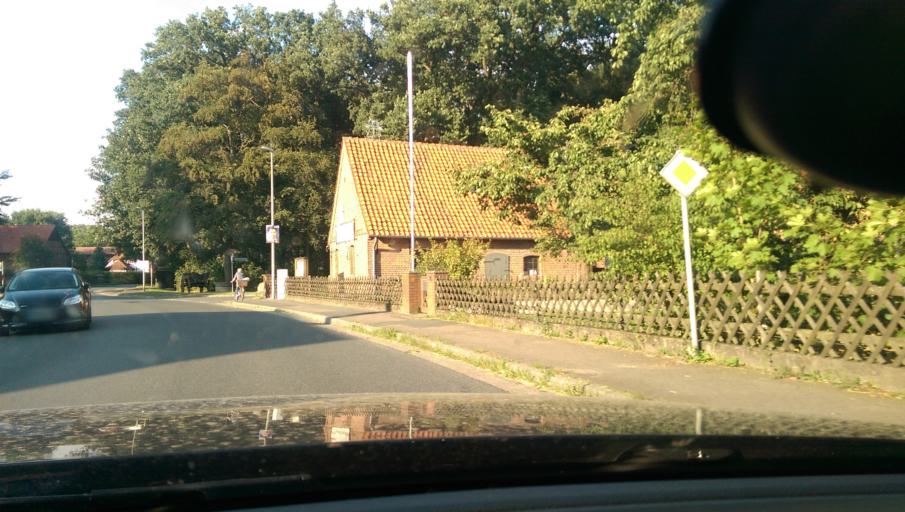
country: DE
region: Lower Saxony
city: Schwarmstedt
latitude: 52.5861
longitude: 9.5869
